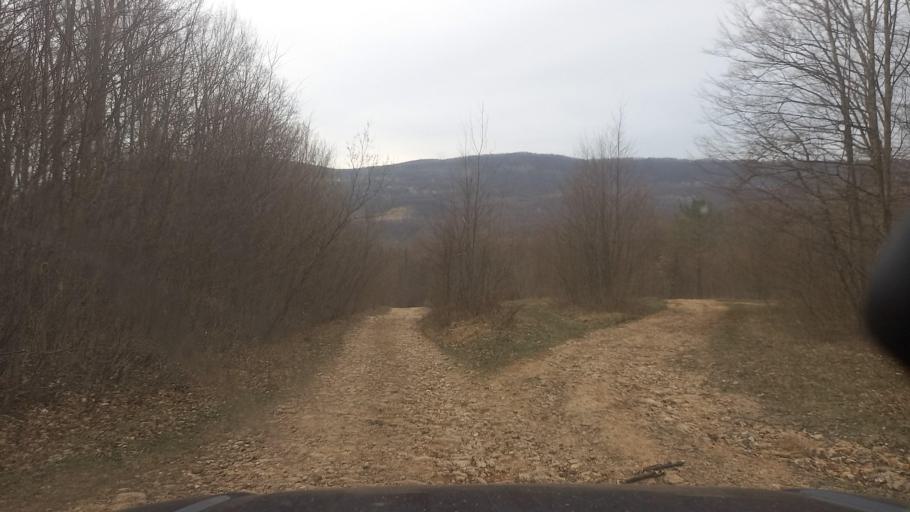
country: RU
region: Adygeya
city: Kamennomostskiy
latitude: 44.1896
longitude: 39.9674
